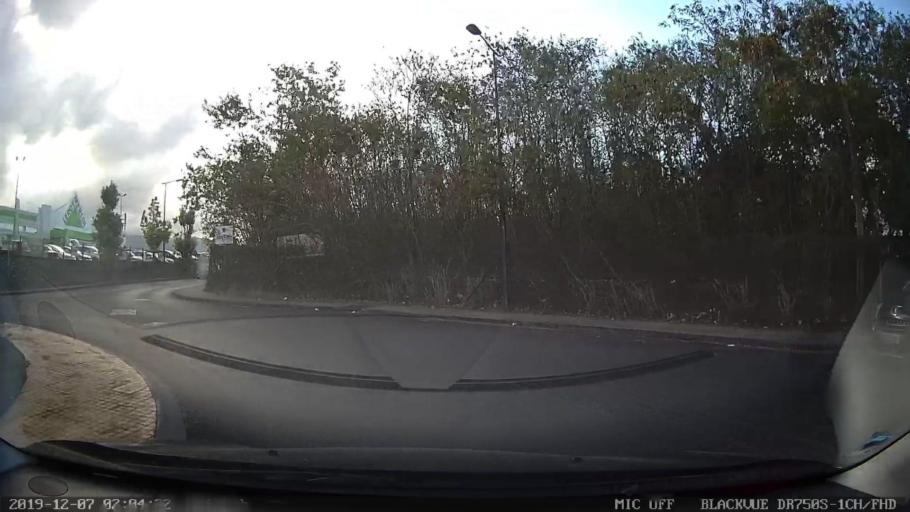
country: RE
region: Reunion
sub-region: Reunion
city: Sainte-Marie
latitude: -20.9016
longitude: 55.5188
